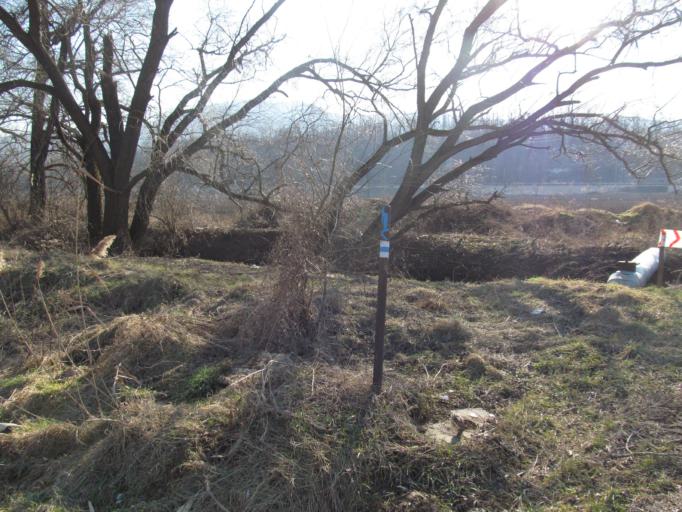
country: HU
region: Pest
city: Pilisborosjeno
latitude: 47.5916
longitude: 18.9829
